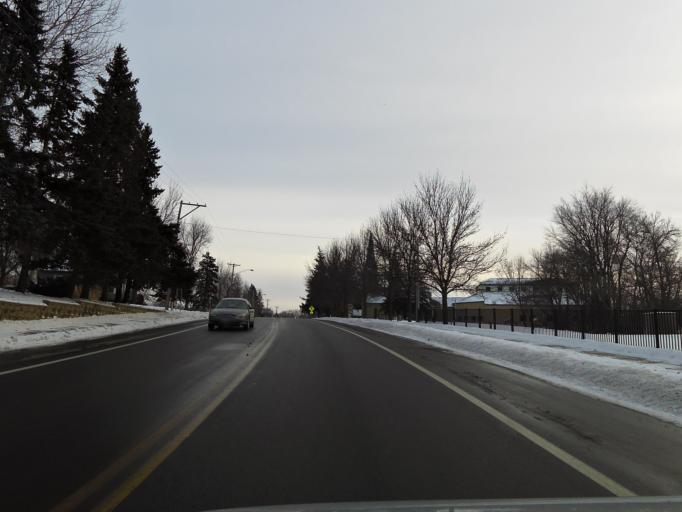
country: US
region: Minnesota
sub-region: Carver County
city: Victoria
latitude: 44.8563
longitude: -93.6618
